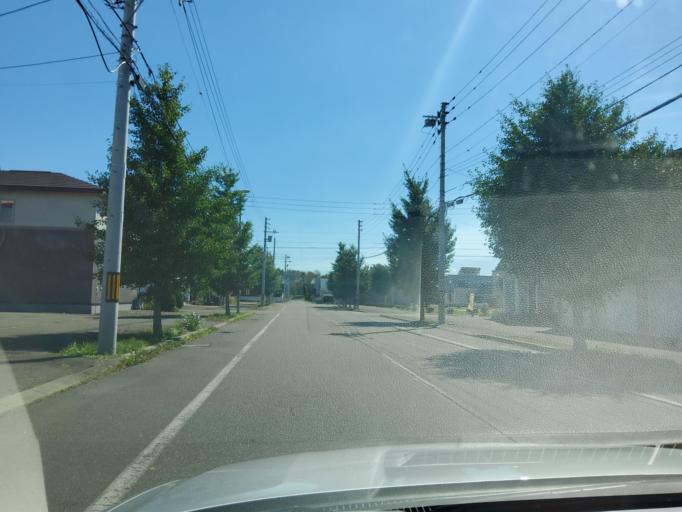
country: JP
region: Hokkaido
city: Obihiro
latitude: 42.9418
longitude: 143.2198
